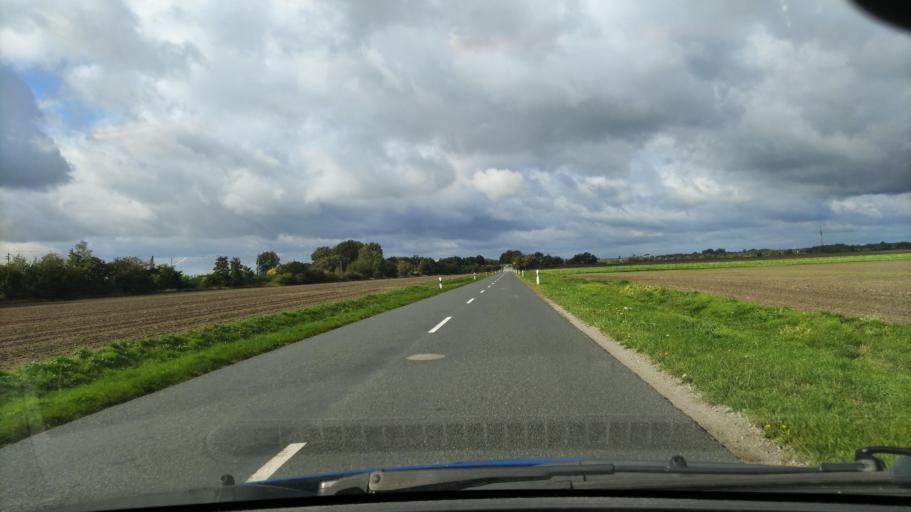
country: DE
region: Saxony-Anhalt
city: Salzwedel
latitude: 52.8538
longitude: 11.1961
